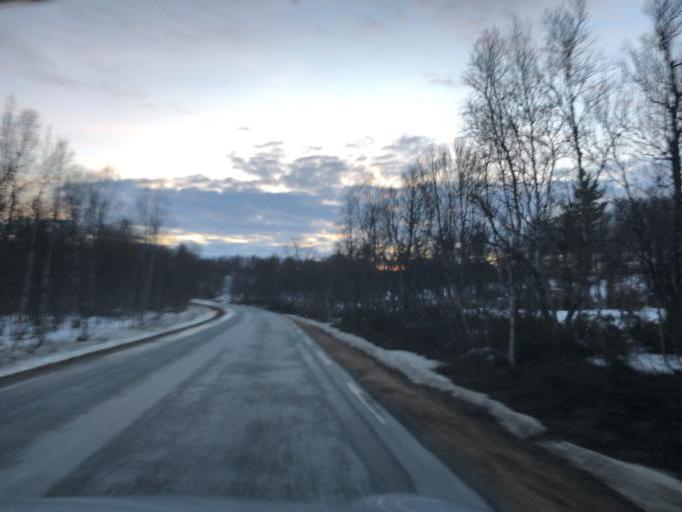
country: NO
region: Sor-Trondelag
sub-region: Tydal
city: Aas
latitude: 62.6748
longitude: 11.8039
